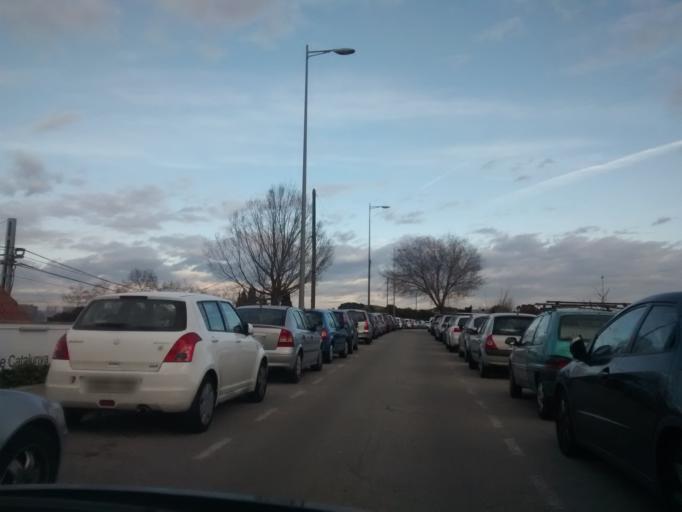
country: ES
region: Catalonia
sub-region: Provincia de Barcelona
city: Rubi
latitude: 41.4760
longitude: 2.0464
